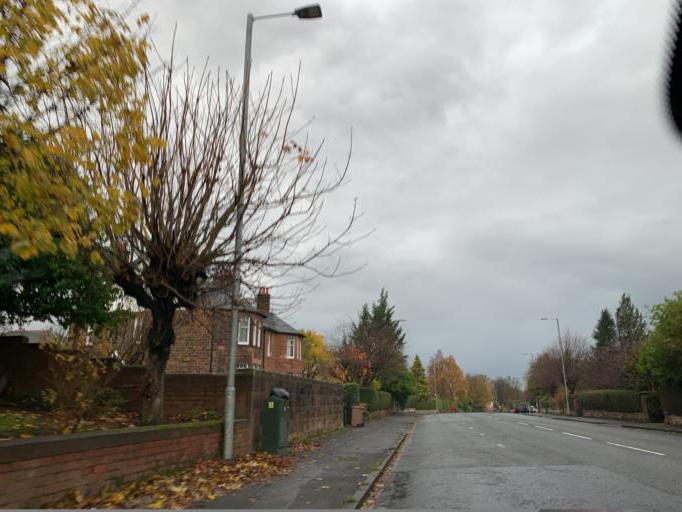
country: GB
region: Scotland
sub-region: East Renfrewshire
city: Giffnock
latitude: 55.8152
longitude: -4.2848
